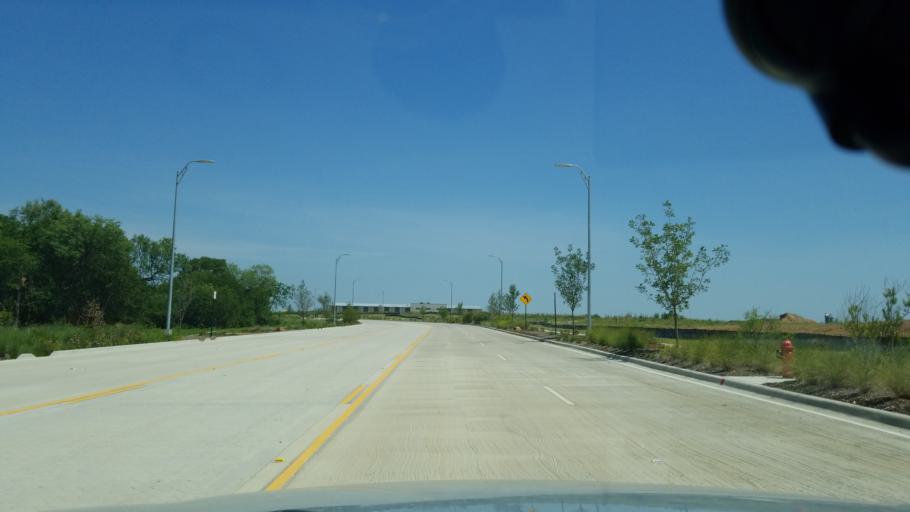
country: US
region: Texas
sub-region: Tarrant County
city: Euless
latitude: 32.8471
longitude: -97.0309
